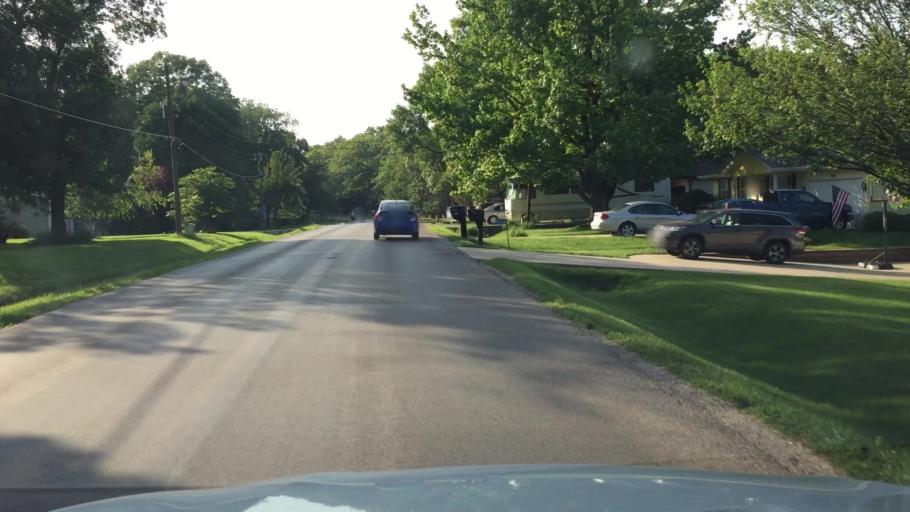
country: US
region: Iowa
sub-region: Linn County
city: Ely
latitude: 41.8283
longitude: -91.6256
